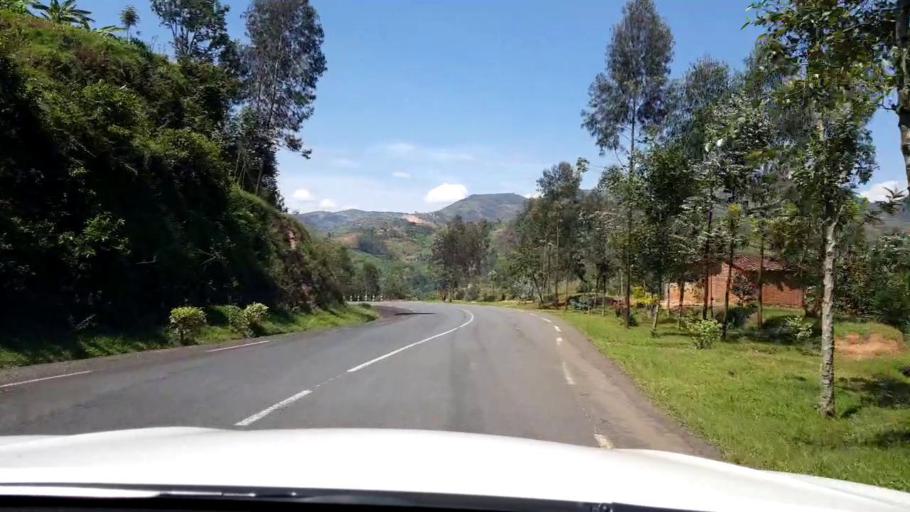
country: RW
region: Southern Province
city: Gitarama
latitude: -1.9136
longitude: 29.6316
